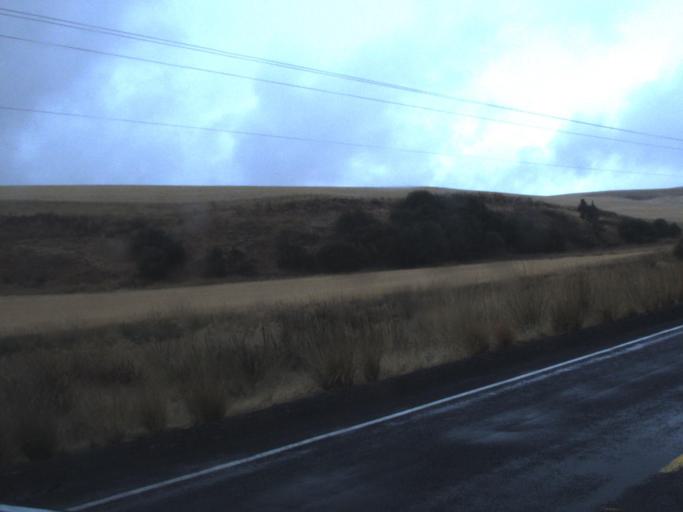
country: US
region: Washington
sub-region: Spokane County
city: Cheney
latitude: 47.1144
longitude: -117.6964
